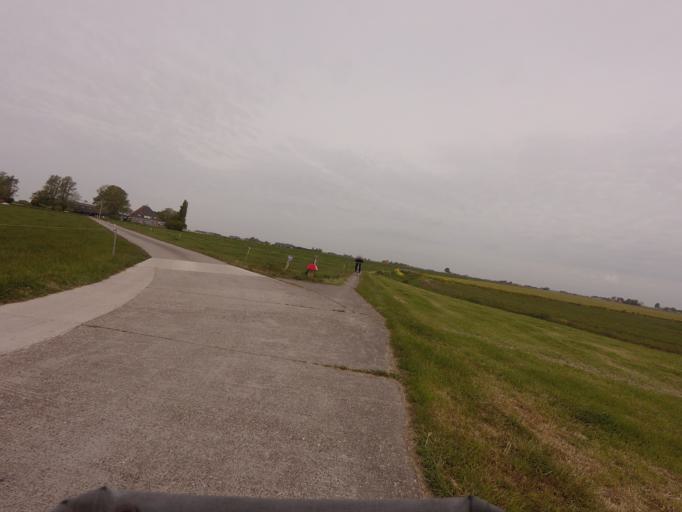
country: NL
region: Friesland
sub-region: Sudwest Fryslan
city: Workum
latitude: 53.0146
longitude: 5.4529
